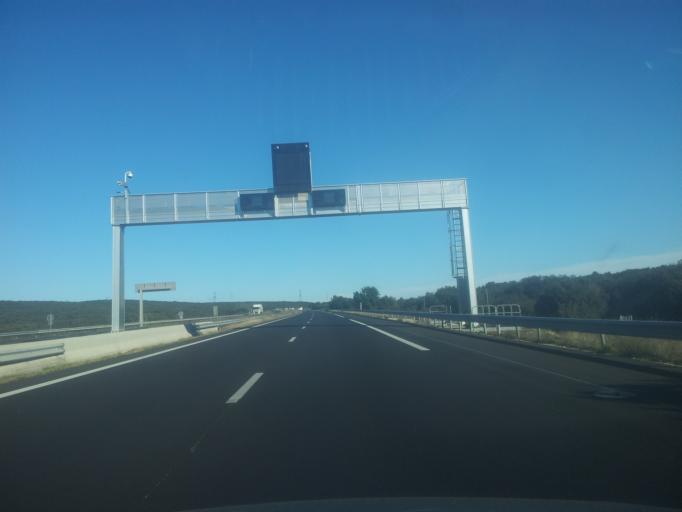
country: FR
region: Languedoc-Roussillon
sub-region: Departement du Gard
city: Saze
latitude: 43.9661
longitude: 4.6412
